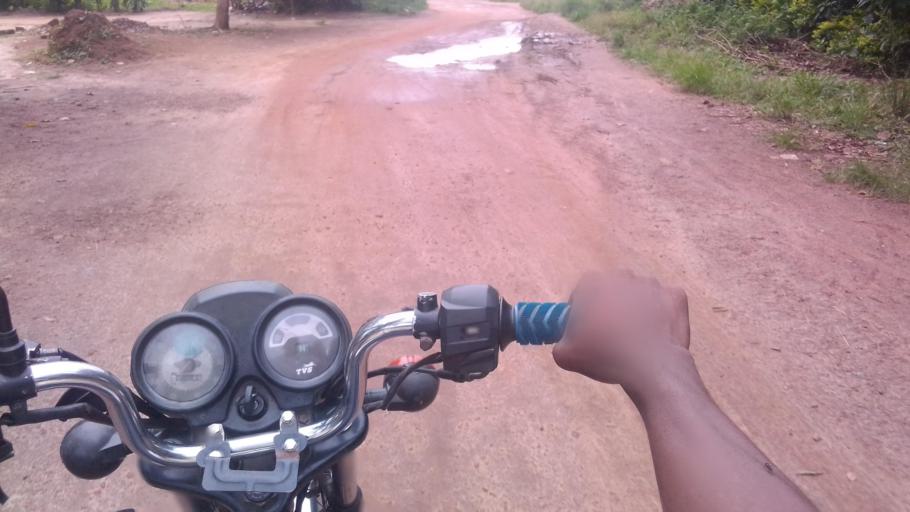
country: SL
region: Eastern Province
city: Kenema
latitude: 7.8673
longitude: -11.1736
